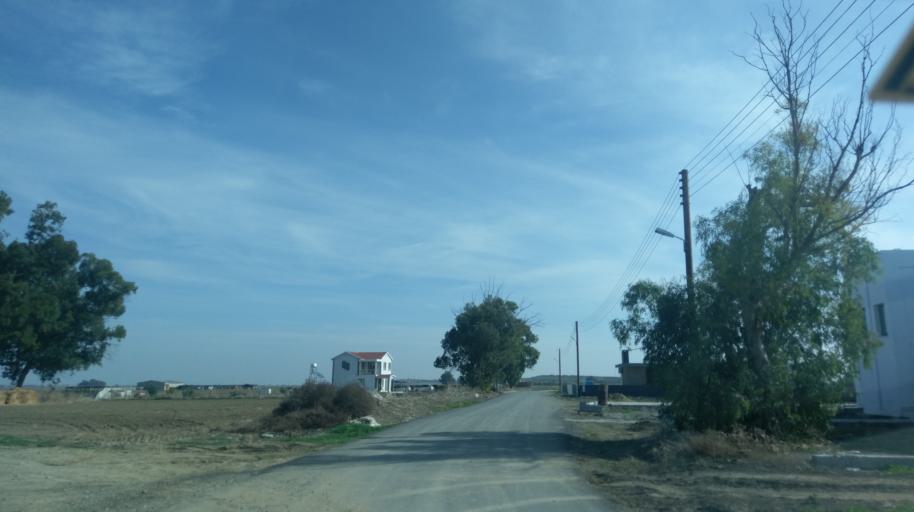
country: CY
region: Ammochostos
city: Lefkonoiko
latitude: 35.1677
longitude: 33.6411
